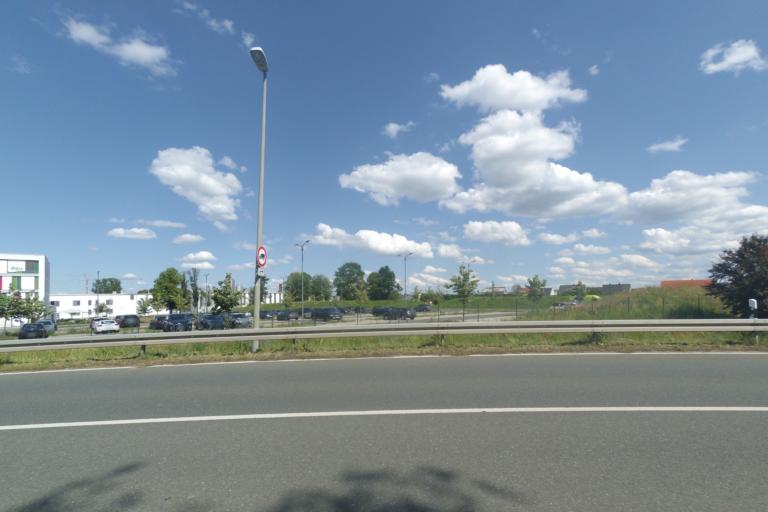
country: DE
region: Bavaria
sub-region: Regierungsbezirk Mittelfranken
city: Adelsdorf
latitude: 49.7103
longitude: 10.8836
